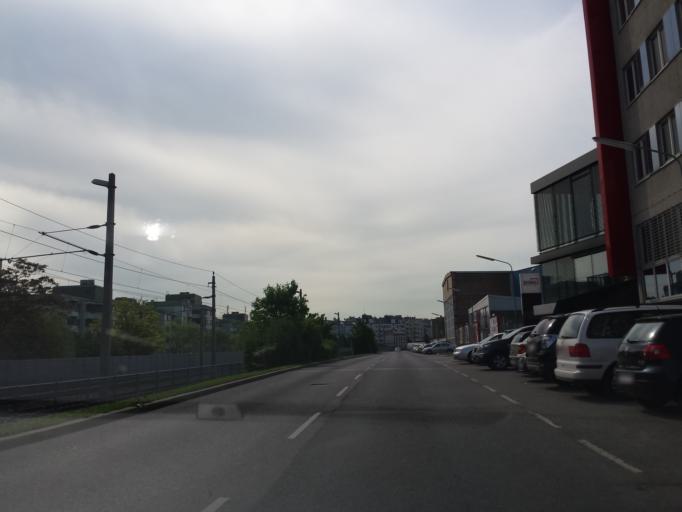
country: AT
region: Vienna
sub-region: Wien Stadt
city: Vienna
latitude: 48.1811
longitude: 16.4062
